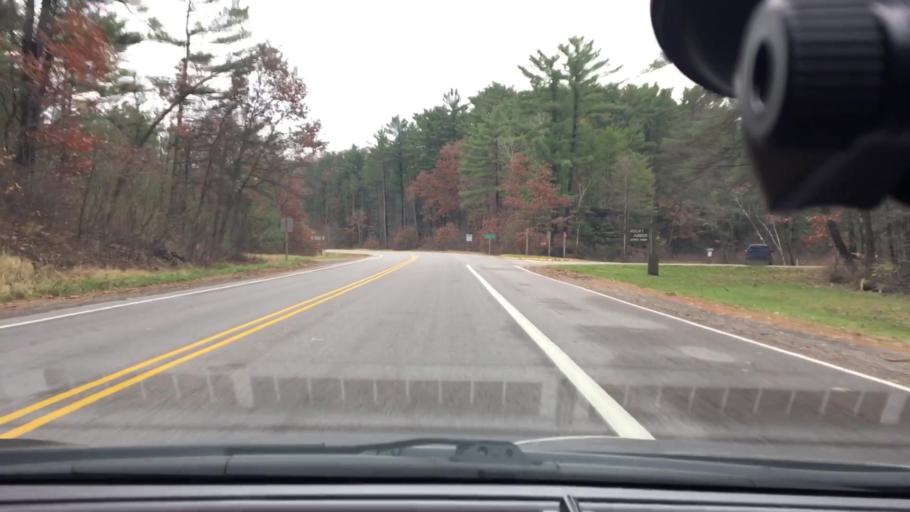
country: US
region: Wisconsin
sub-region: Columbia County
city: Wisconsin Dells
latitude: 43.6415
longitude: -89.8023
